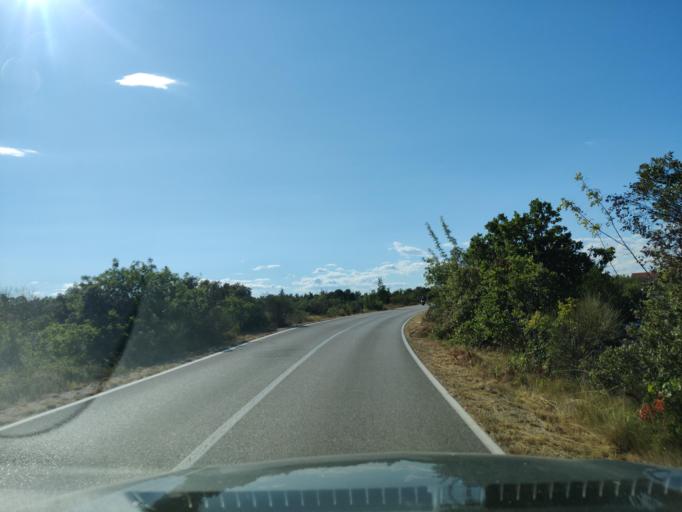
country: HR
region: Sibensko-Kniniska
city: Zaton
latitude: 43.7452
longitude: 15.8473
